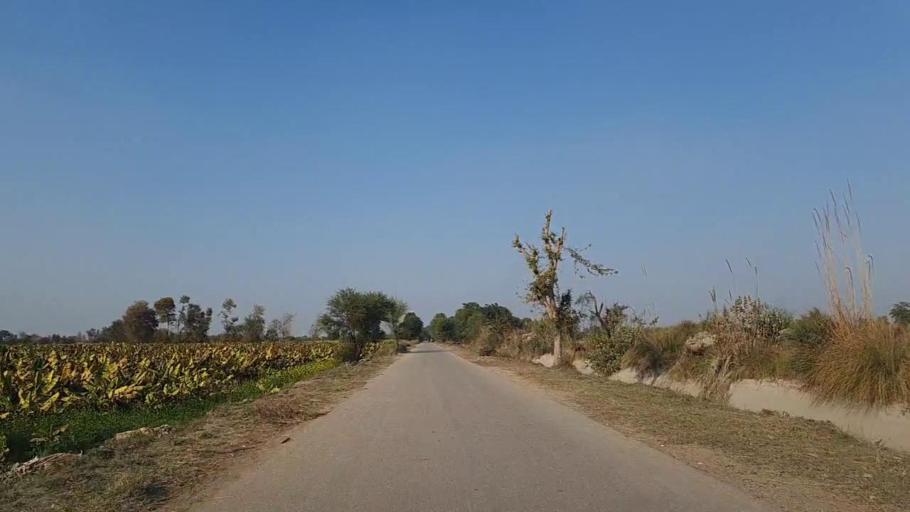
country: PK
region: Sindh
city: Daur
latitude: 26.4095
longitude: 68.2592
